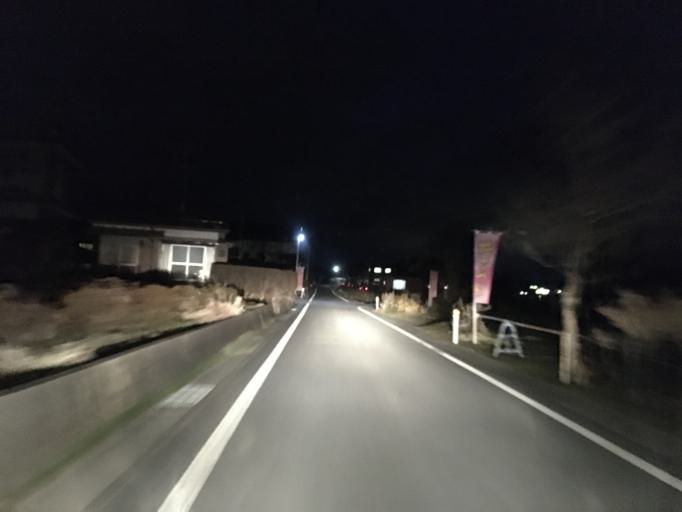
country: JP
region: Iwate
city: Ichinoseki
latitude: 38.8214
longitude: 141.1902
